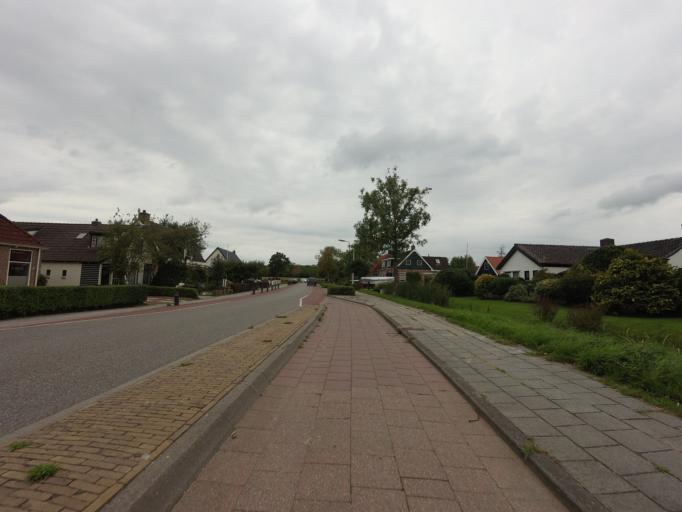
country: NL
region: Friesland
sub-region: Sudwest Fryslan
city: Sneek
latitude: 53.0401
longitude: 5.6389
